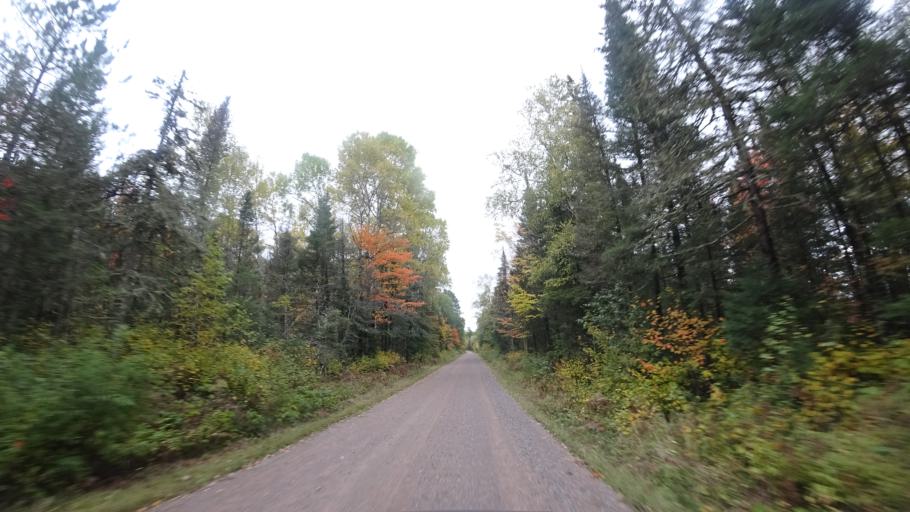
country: US
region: Wisconsin
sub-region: Sawyer County
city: Little Round Lake
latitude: 46.0720
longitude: -90.9935
